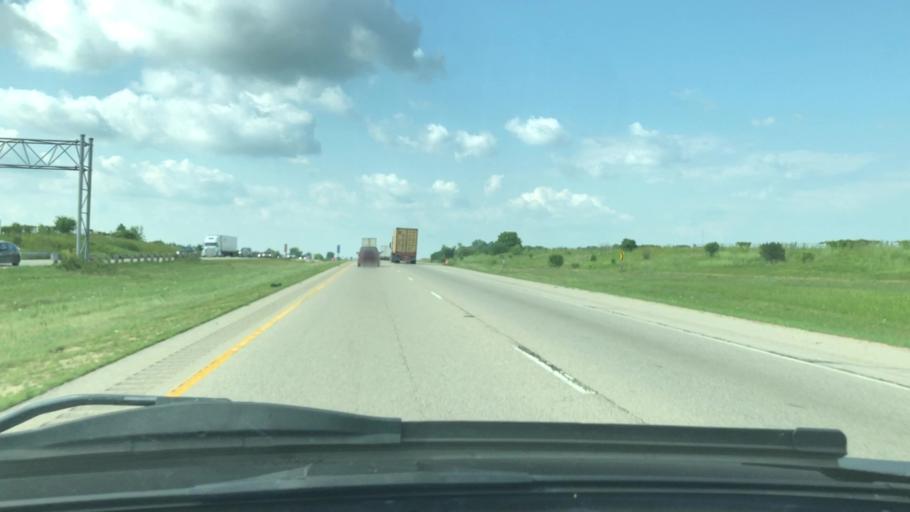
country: US
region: Wisconsin
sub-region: Rock County
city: Beloit
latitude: 42.5296
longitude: -88.9751
